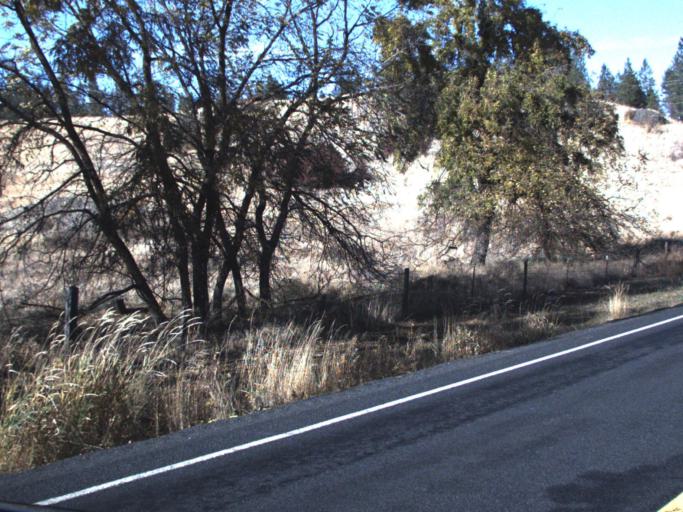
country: US
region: Washington
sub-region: Lincoln County
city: Davenport
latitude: 47.8841
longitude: -118.2644
